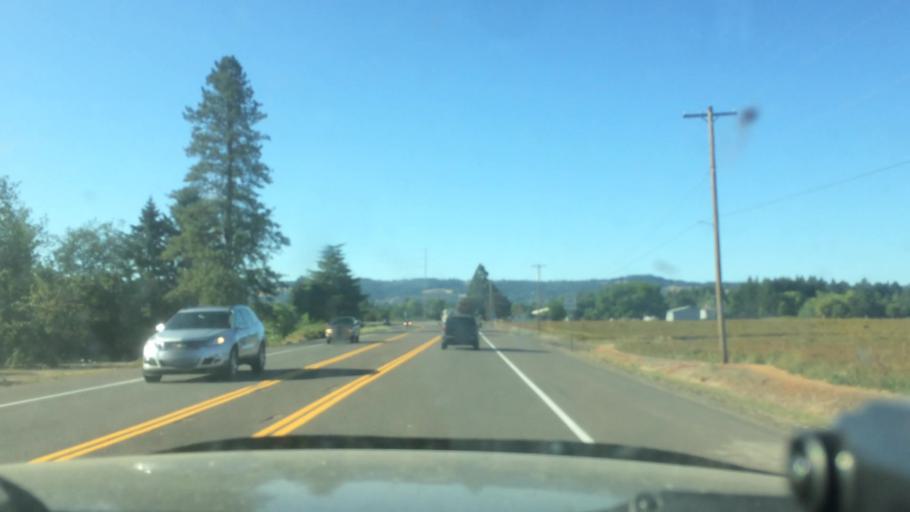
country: US
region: Oregon
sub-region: Yamhill County
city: Newberg
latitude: 45.2832
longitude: -122.9442
